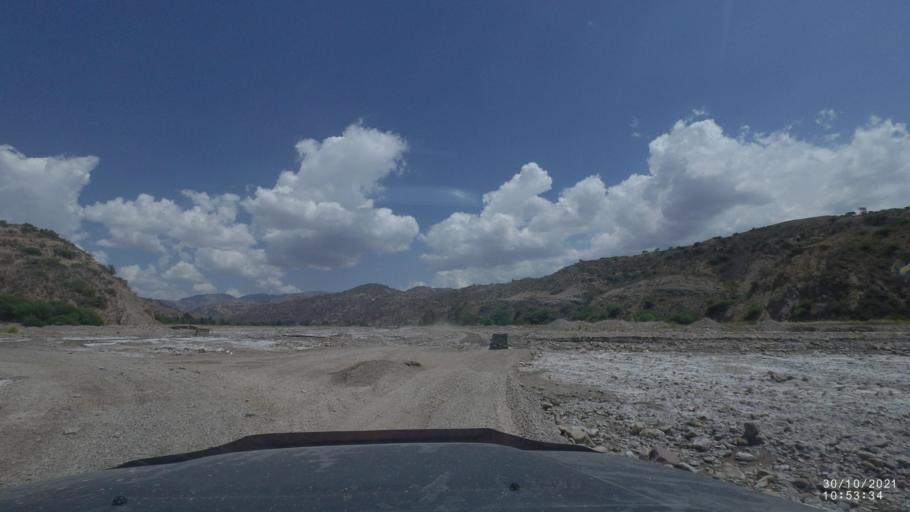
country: BO
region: Cochabamba
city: Sipe Sipe
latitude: -17.5483
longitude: -66.4832
